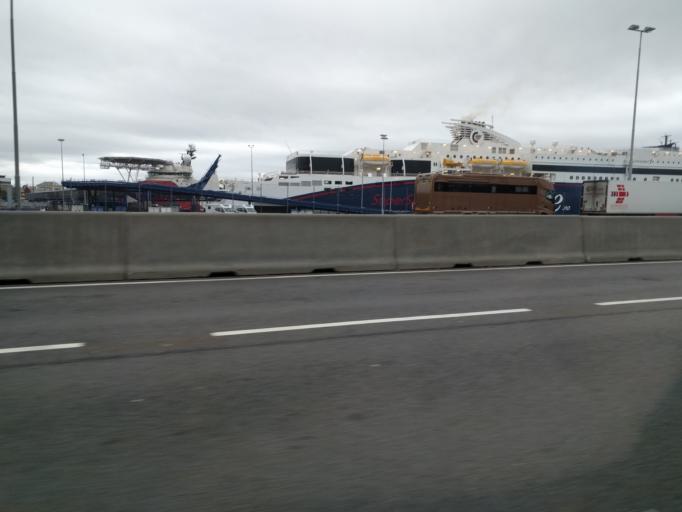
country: NO
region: Vest-Agder
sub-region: Kristiansand
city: Kristiansand
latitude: 58.1436
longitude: 7.9827
